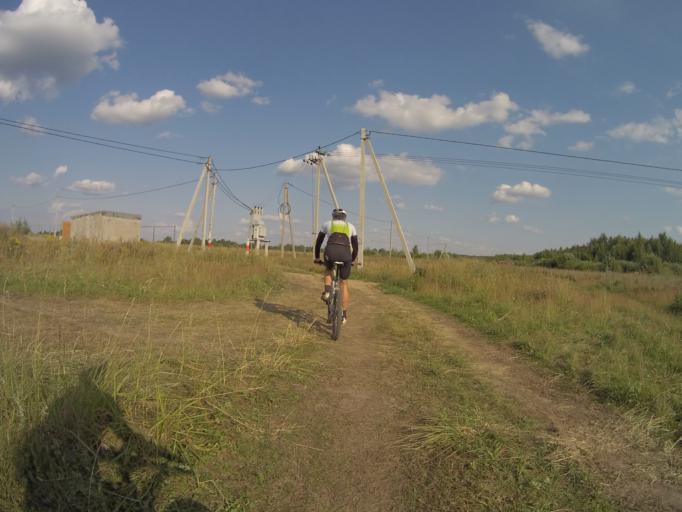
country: RU
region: Vladimir
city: Orgtrud
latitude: 56.1509
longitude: 40.6040
